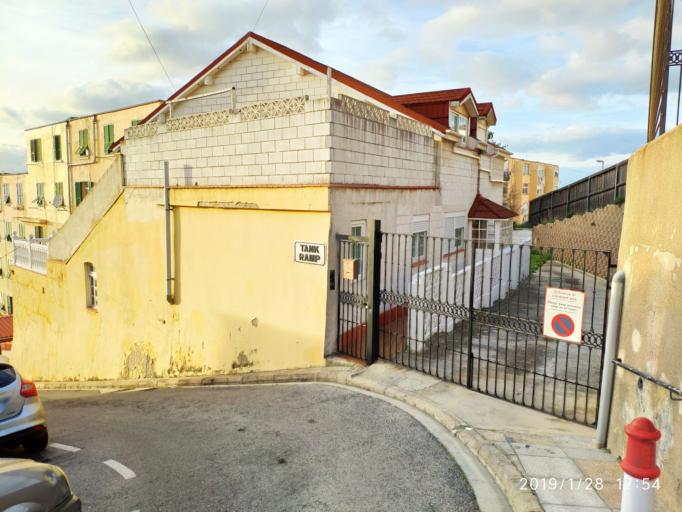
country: GI
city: Gibraltar
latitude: 36.1424
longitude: -5.3501
